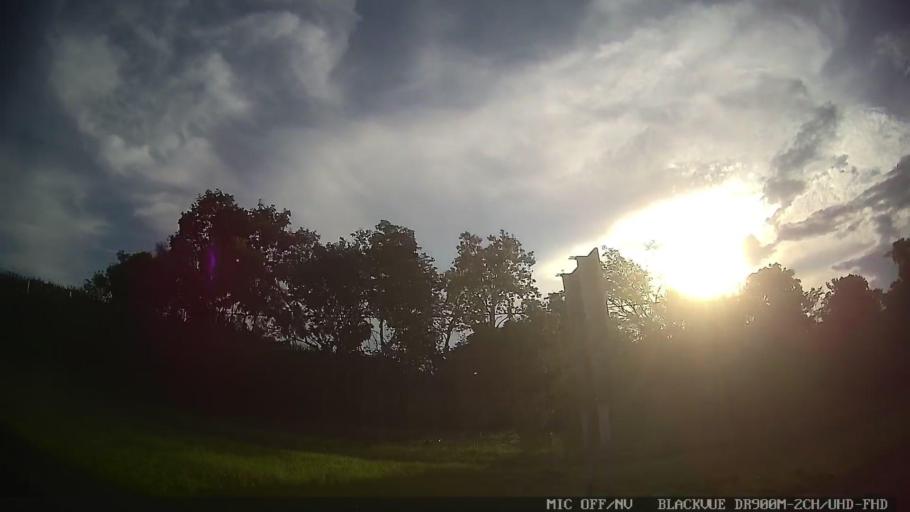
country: BR
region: Sao Paulo
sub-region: Tiete
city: Tiete
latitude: -23.1491
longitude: -47.6660
